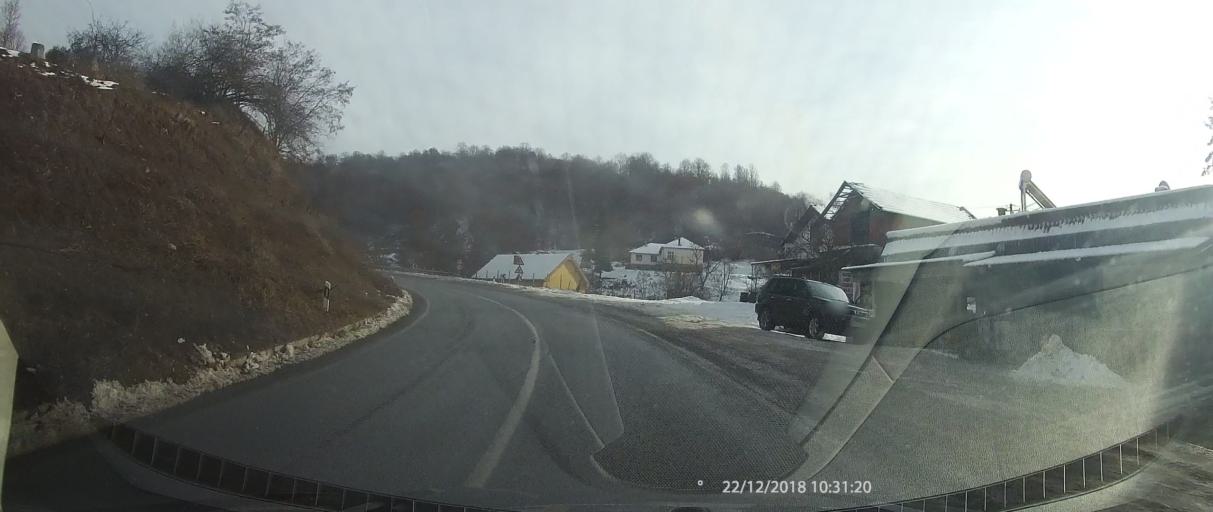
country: MK
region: Kriva Palanka
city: Kriva Palanka
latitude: 42.2226
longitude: 22.4239
